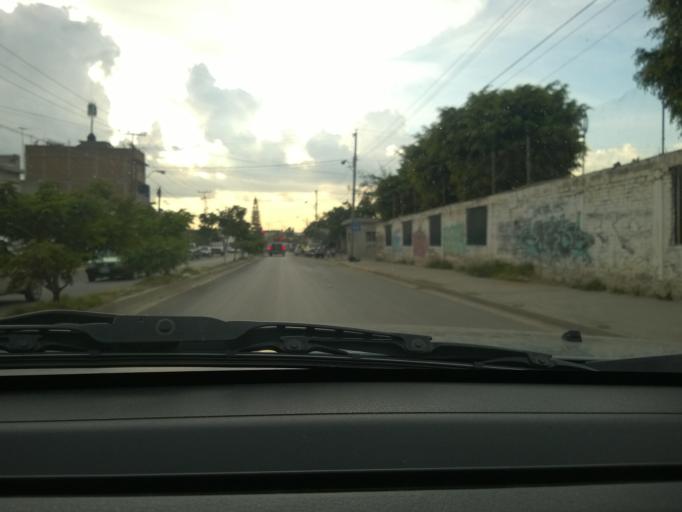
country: MX
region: Guanajuato
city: Leon
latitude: 21.1376
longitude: -101.6479
